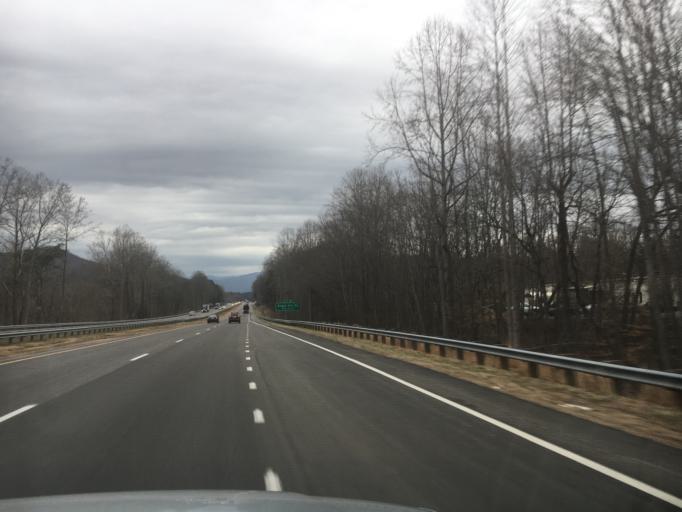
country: US
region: North Carolina
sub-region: McDowell County
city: West Marion
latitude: 35.6346
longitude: -82.0067
